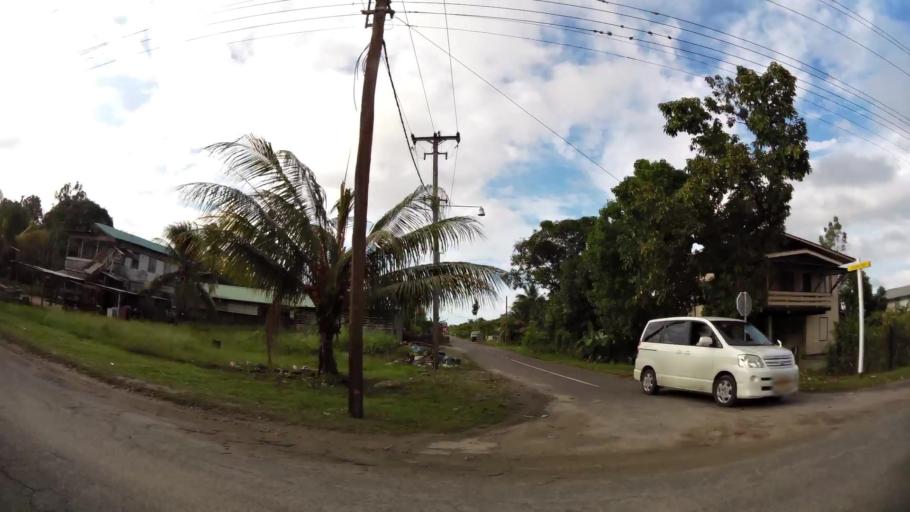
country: SR
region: Paramaribo
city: Paramaribo
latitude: 5.8481
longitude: -55.2434
